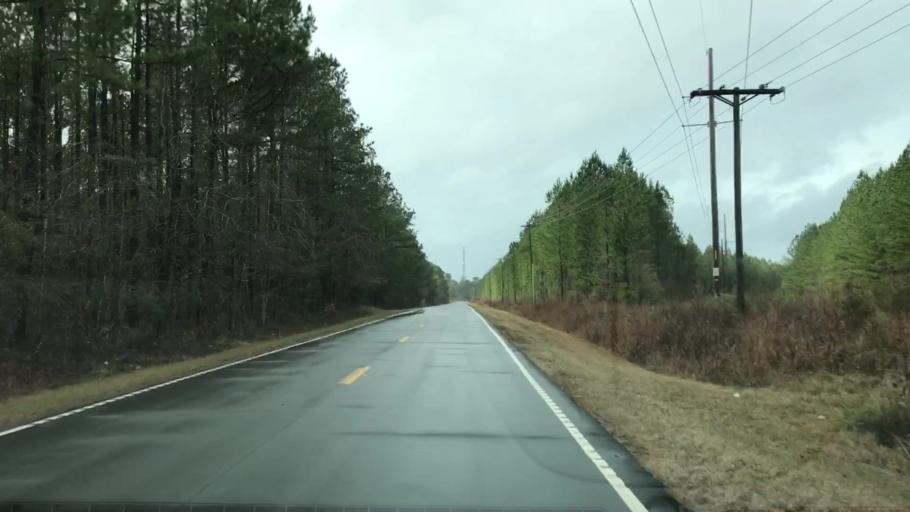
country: US
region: South Carolina
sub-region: Florence County
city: Johnsonville
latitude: 33.6762
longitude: -79.3432
